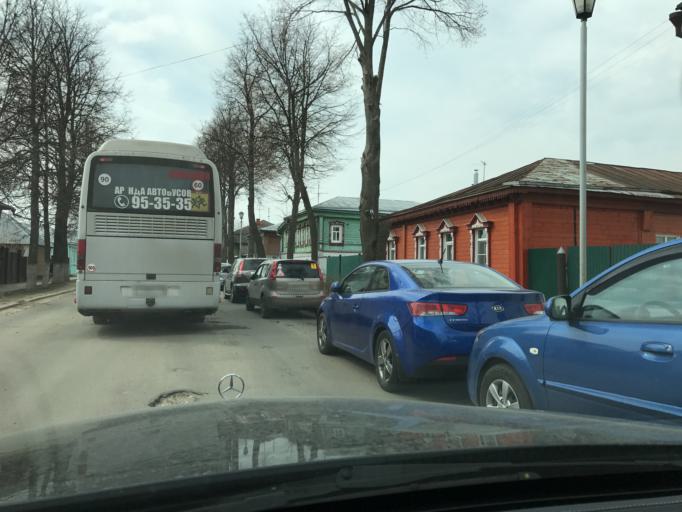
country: RU
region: Vladimir
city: Suzdal'
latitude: 56.4199
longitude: 40.4561
